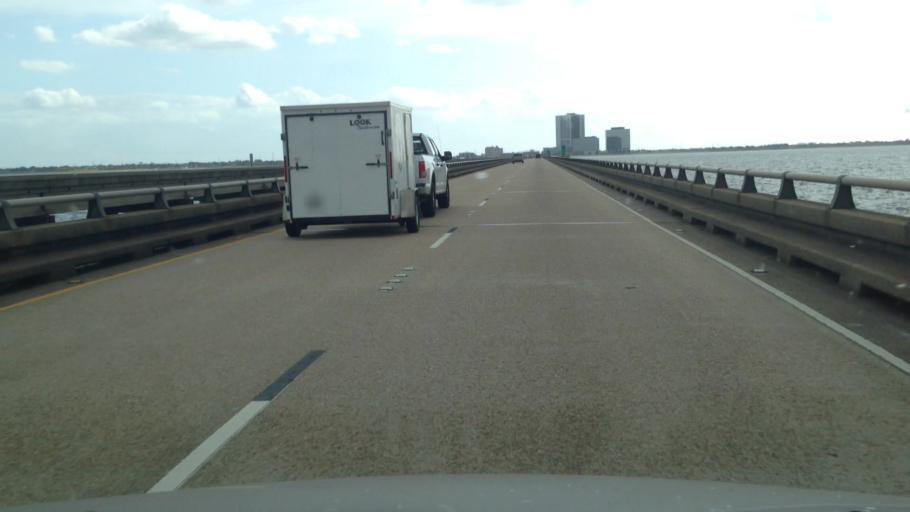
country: US
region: Louisiana
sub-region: Jefferson Parish
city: Metairie
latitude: 30.0430
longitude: -90.1504
